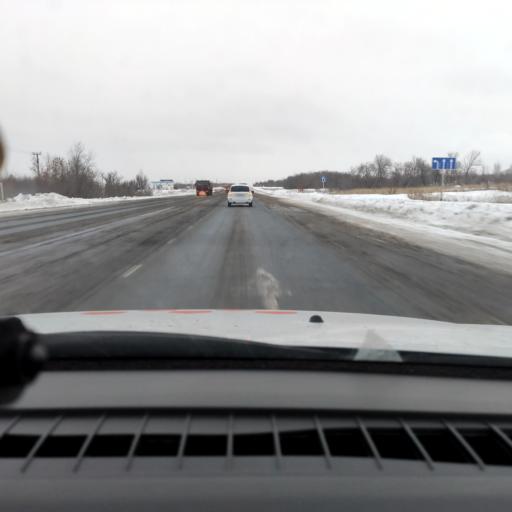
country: RU
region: Samara
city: Chapayevsk
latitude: 52.9534
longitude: 49.7355
